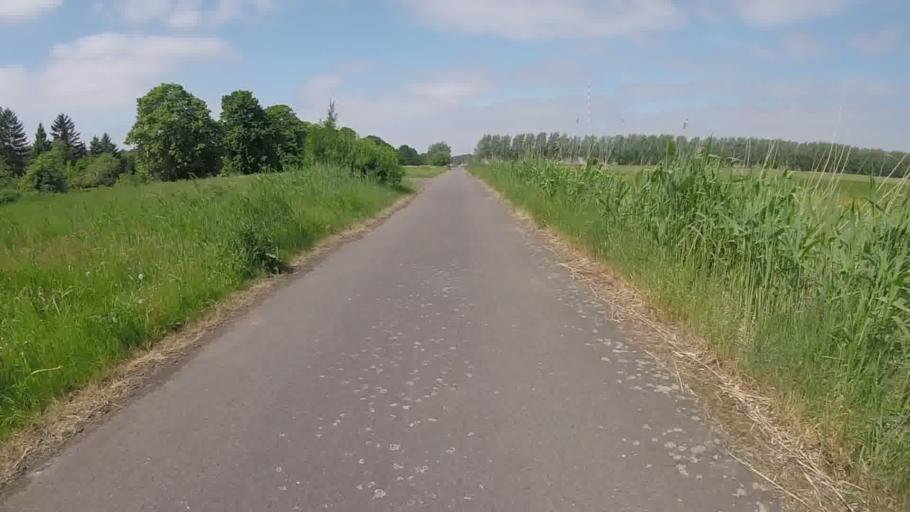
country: DE
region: Hamburg
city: Wandsbek
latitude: 53.5069
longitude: 10.1166
